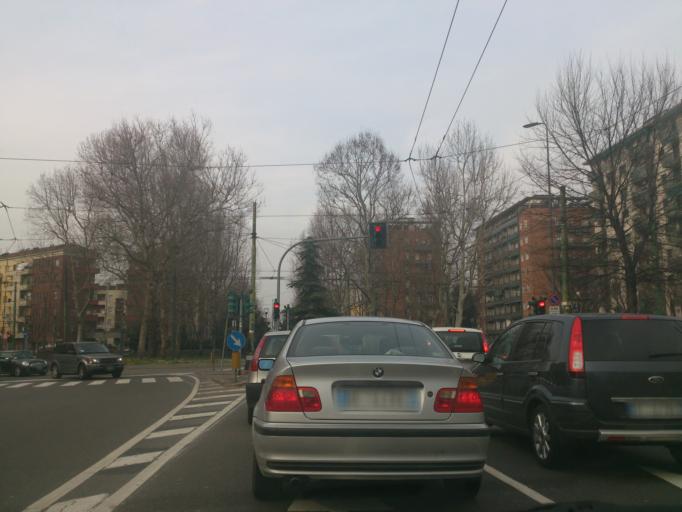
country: IT
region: Lombardy
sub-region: Citta metropolitana di Milano
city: Chiaravalle
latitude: 45.4502
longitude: 9.2241
